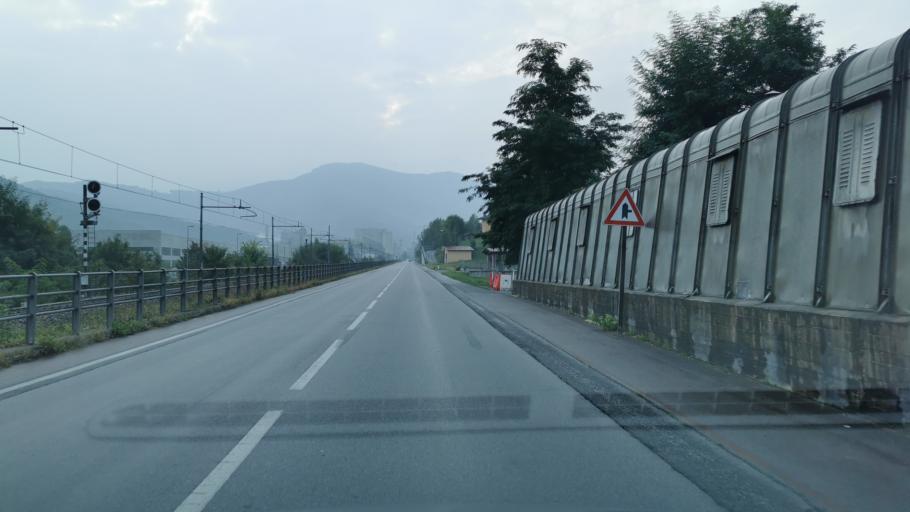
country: IT
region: Piedmont
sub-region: Provincia di Cuneo
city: Roccavione
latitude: 44.3081
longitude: 7.4935
